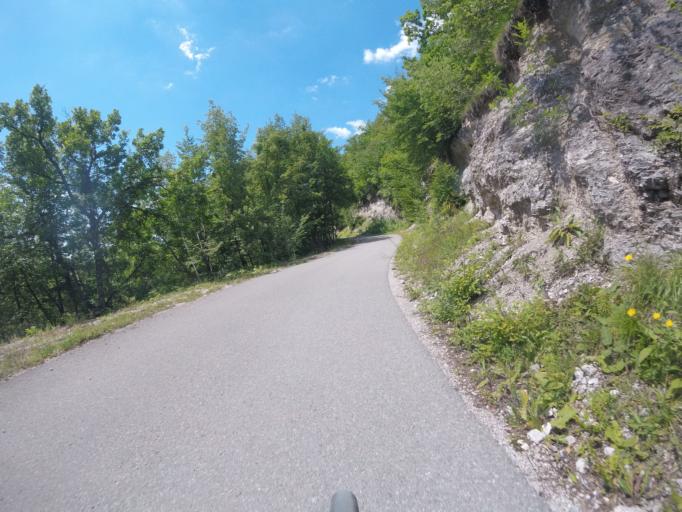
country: SI
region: Kostanjevica na Krki
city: Kostanjevica na Krki
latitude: 45.7659
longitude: 15.4113
